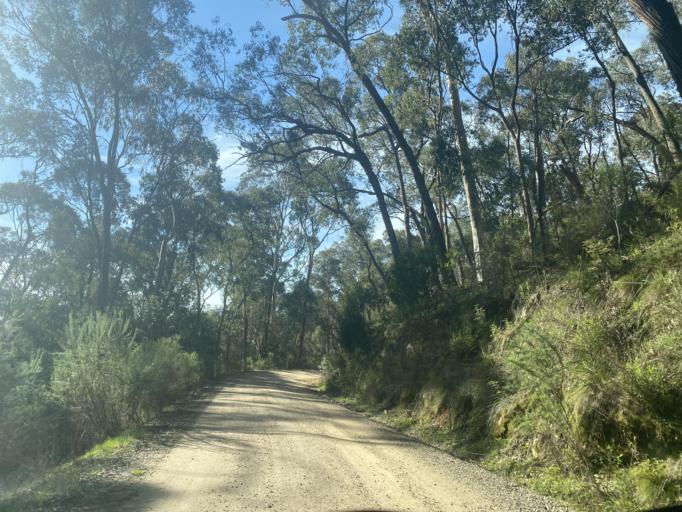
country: AU
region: Victoria
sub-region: Mansfield
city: Mansfield
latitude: -36.8362
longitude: 146.1681
